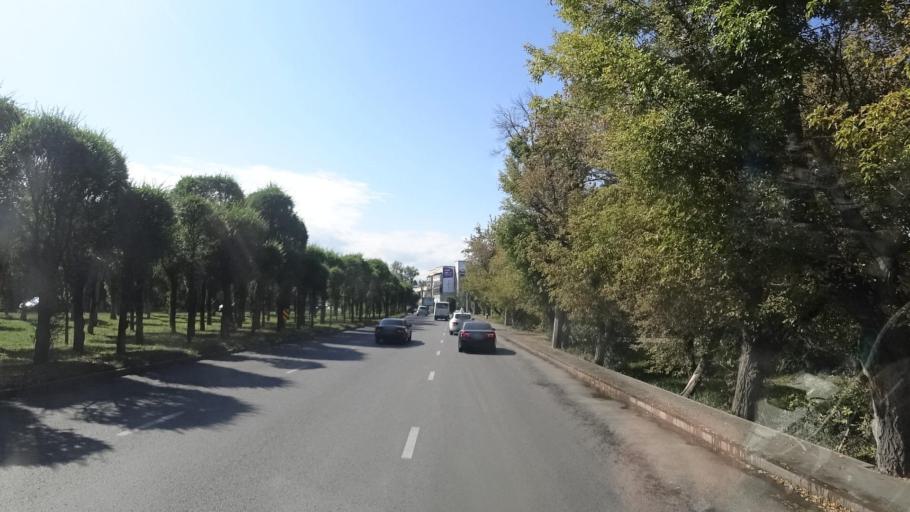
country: KZ
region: Almaty Oblysy
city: Pervomayskiy
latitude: 43.3329
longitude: 76.9790
